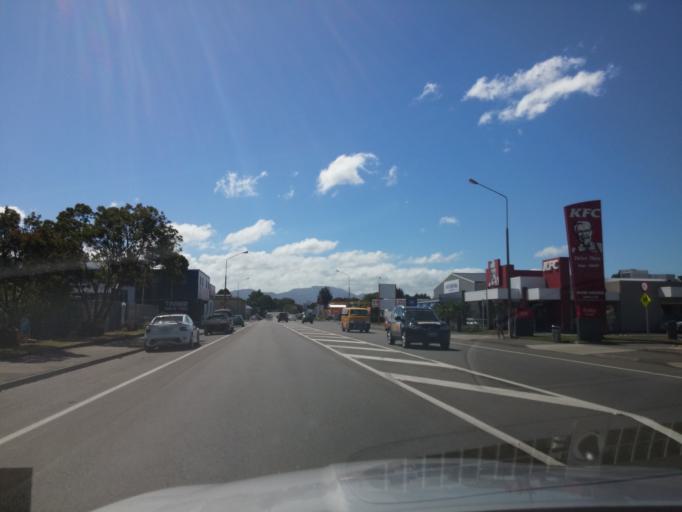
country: NZ
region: Marlborough
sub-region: Marlborough District
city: Blenheim
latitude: -41.5045
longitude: 173.9602
